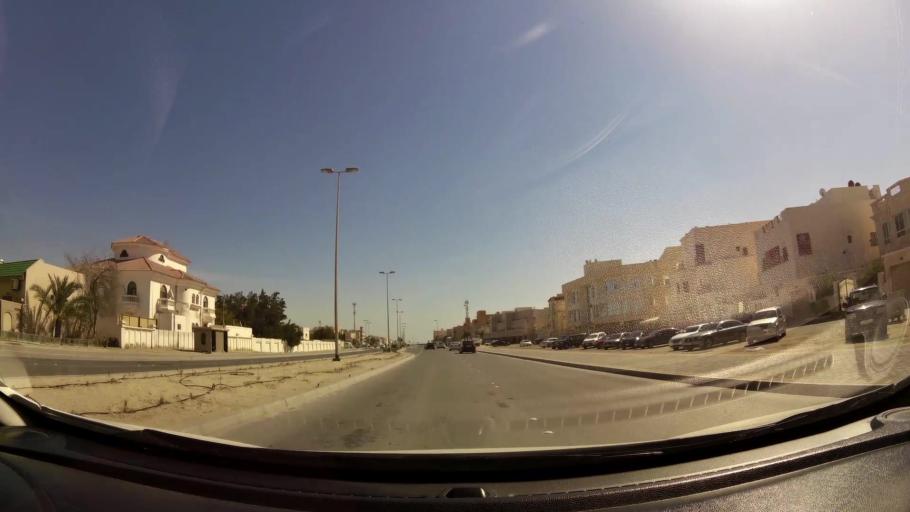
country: BH
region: Muharraq
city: Al Hadd
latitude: 26.2525
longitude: 50.6397
